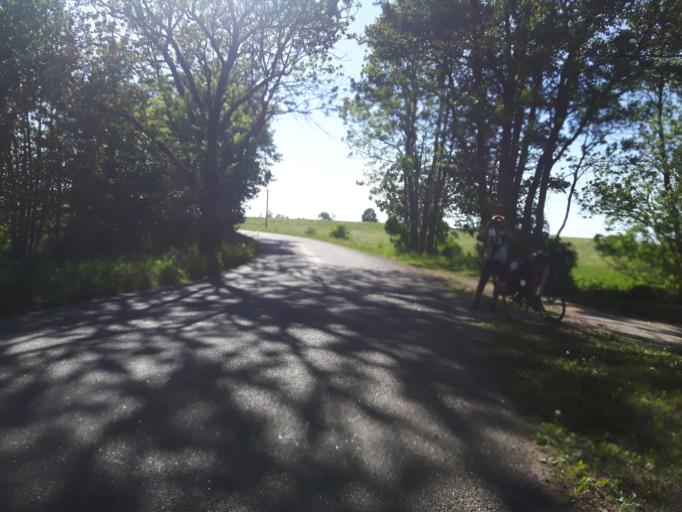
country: EE
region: Laeaene-Virumaa
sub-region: Haljala vald
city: Haljala
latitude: 59.5399
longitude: 26.0728
